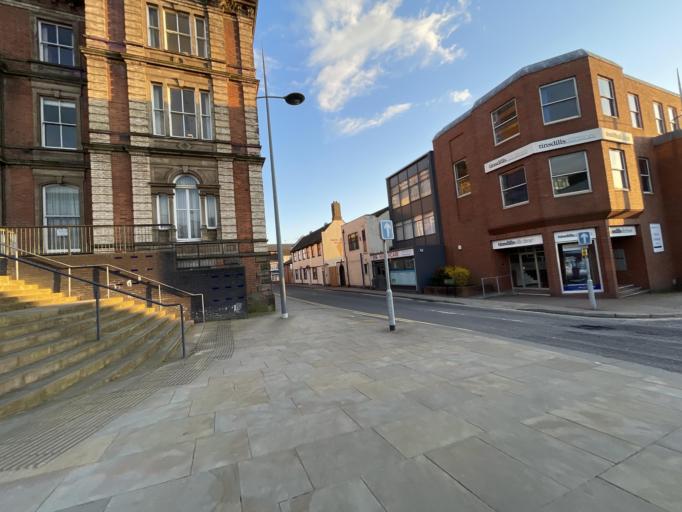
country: GB
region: England
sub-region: Stoke-on-Trent
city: Stoke-on-Trent
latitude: 53.0238
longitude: -2.1758
